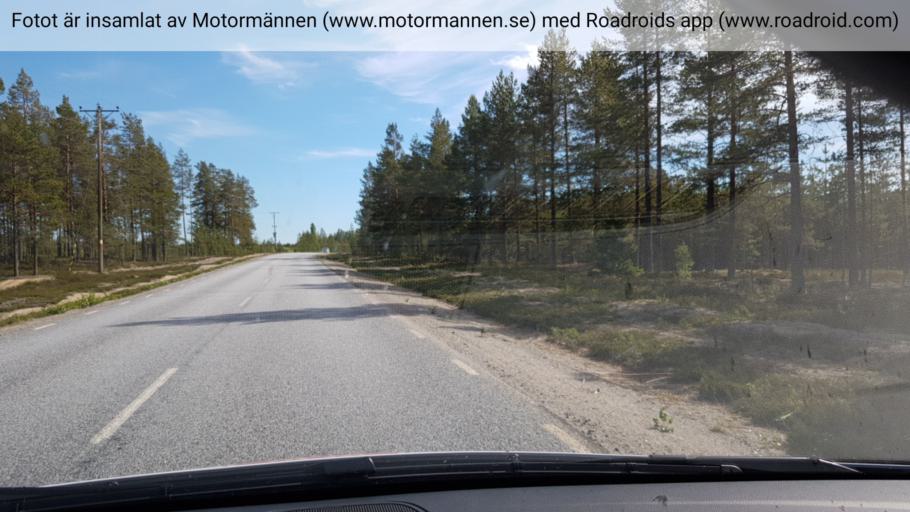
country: SE
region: Vaesterbotten
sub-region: Umea Kommun
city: Saevar
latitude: 63.9421
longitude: 20.5225
